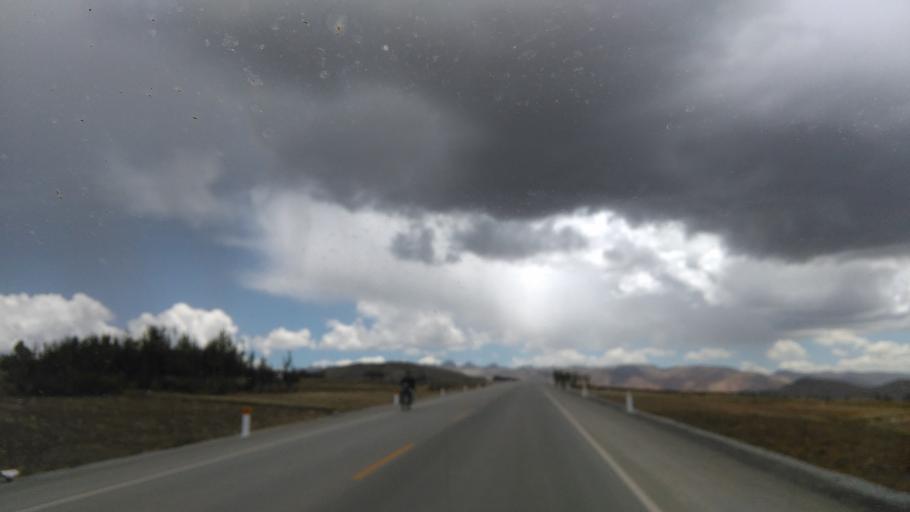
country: PE
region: Apurimac
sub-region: Provincia de Andahuaylas
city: San Jeronimo
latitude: -13.7230
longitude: -73.3509
